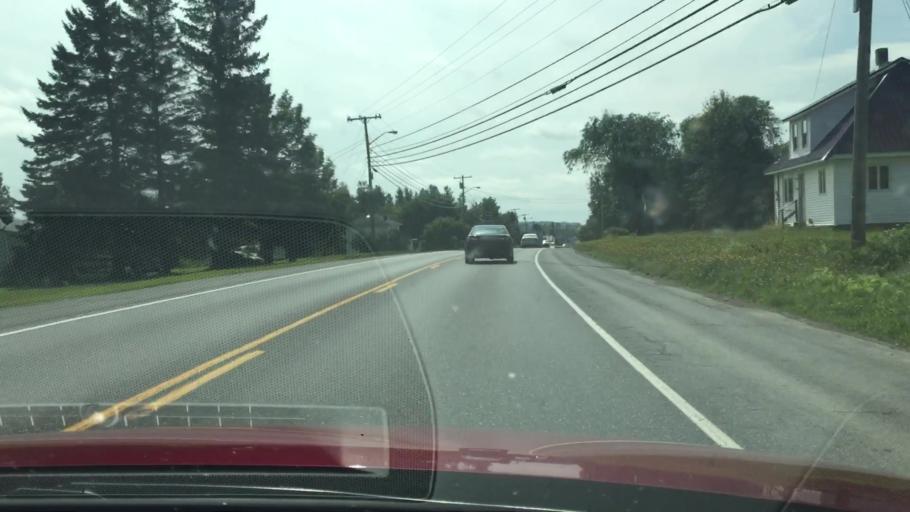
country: US
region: Maine
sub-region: Aroostook County
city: Easton
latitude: 46.4337
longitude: -67.8439
